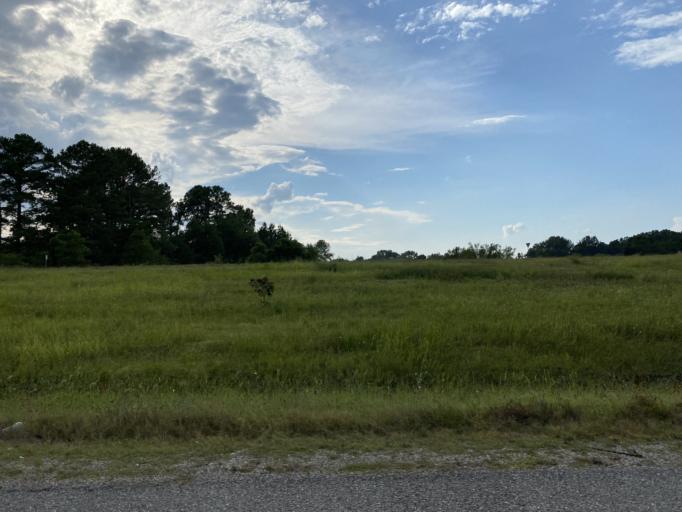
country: US
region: Mississippi
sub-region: Alcorn County
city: Corinth
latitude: 34.9807
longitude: -88.5221
